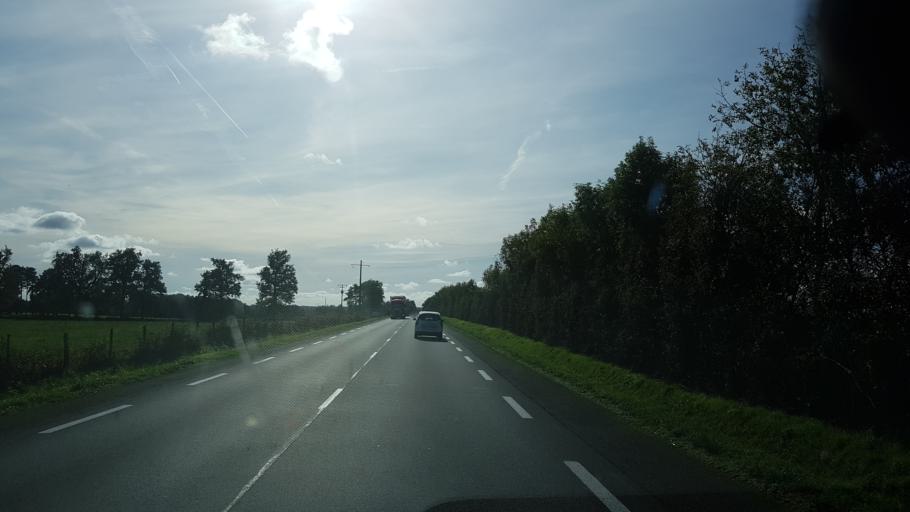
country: FR
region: Poitou-Charentes
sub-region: Departement de la Charente
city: Loubert
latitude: 45.9777
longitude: 0.5977
